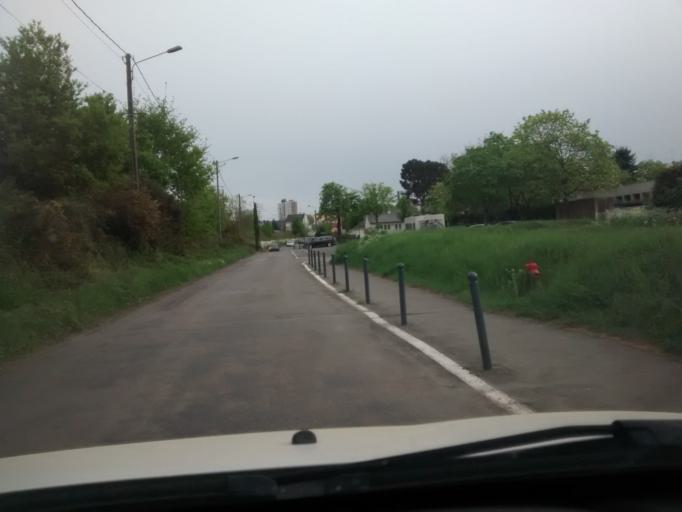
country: FR
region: Brittany
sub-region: Departement d'Ille-et-Vilaine
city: Rennes
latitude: 48.1239
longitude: -1.6886
